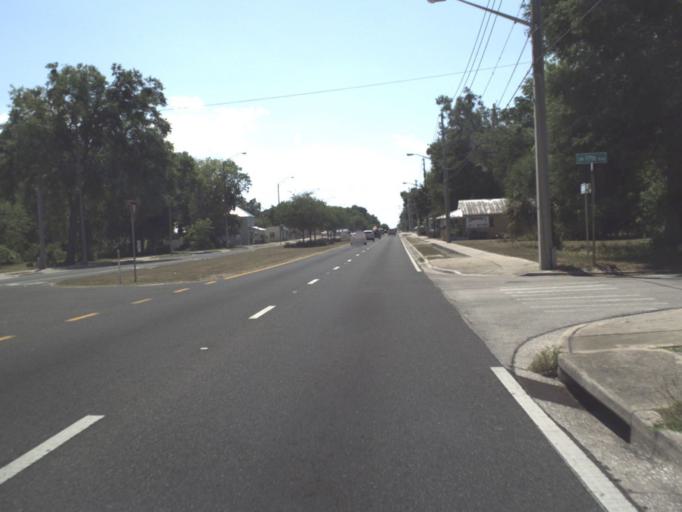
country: US
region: Florida
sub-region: Marion County
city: Ocala
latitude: 29.1862
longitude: -82.1543
